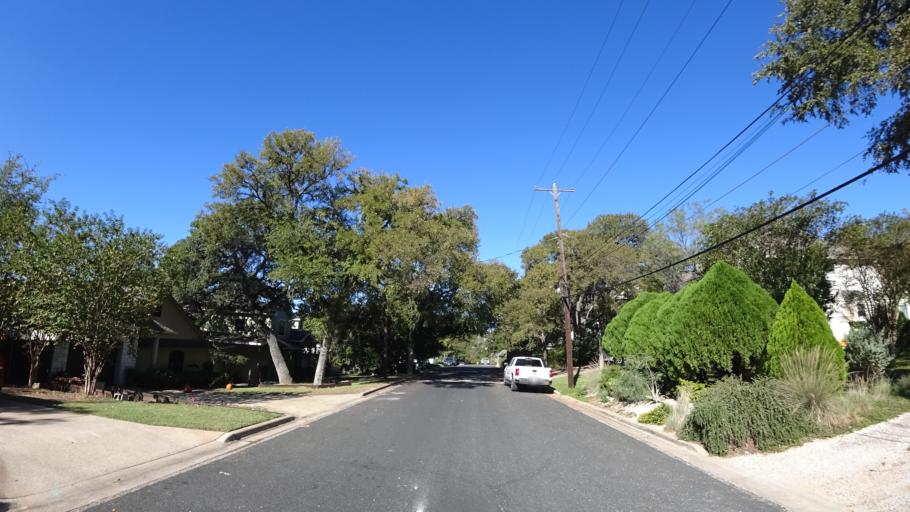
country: US
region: Texas
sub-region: Travis County
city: Rollingwood
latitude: 30.2823
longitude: -97.7680
